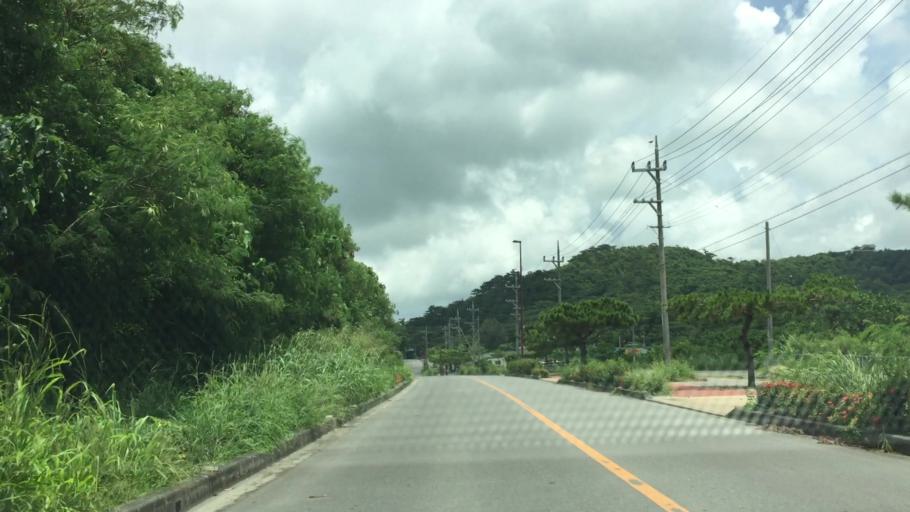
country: JP
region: Okinawa
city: Ishigaki
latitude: 24.3640
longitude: 124.1570
